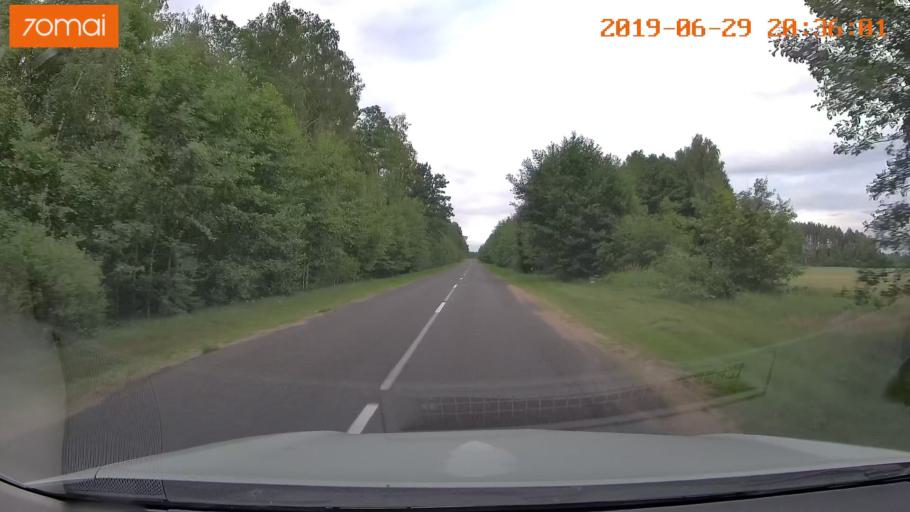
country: BY
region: Brest
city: Hantsavichy
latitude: 52.5216
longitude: 26.3552
